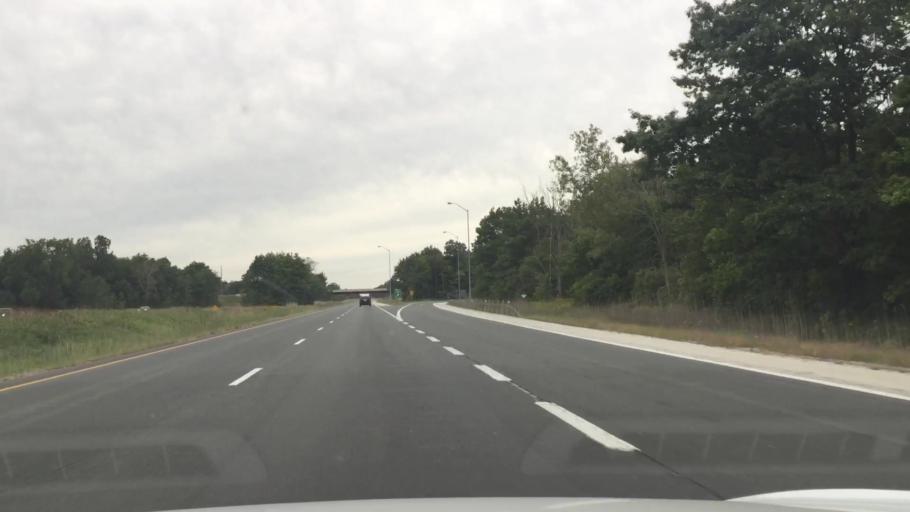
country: CA
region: Ontario
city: Camlachie
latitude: 42.9916
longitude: -81.9972
